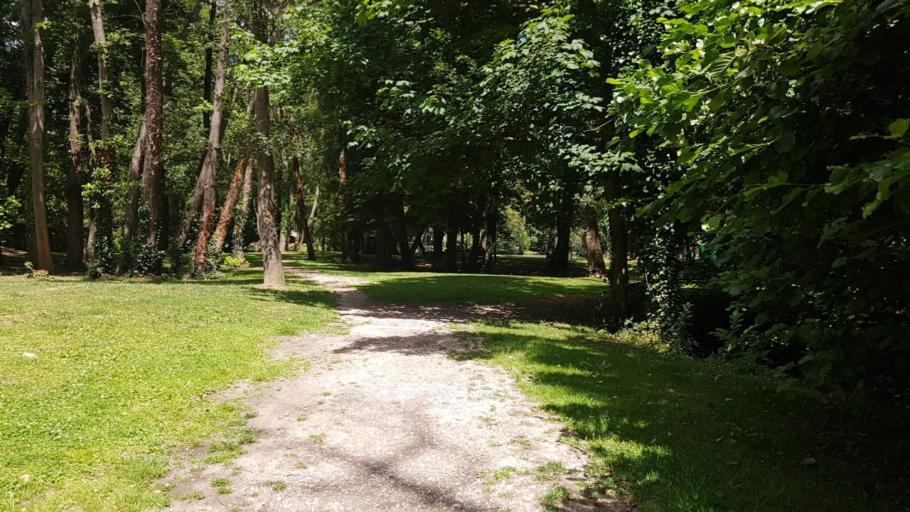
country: FR
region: Ile-de-France
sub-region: Departement de Seine-et-Marne
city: Claye-Souilly
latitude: 48.9614
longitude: 2.6744
